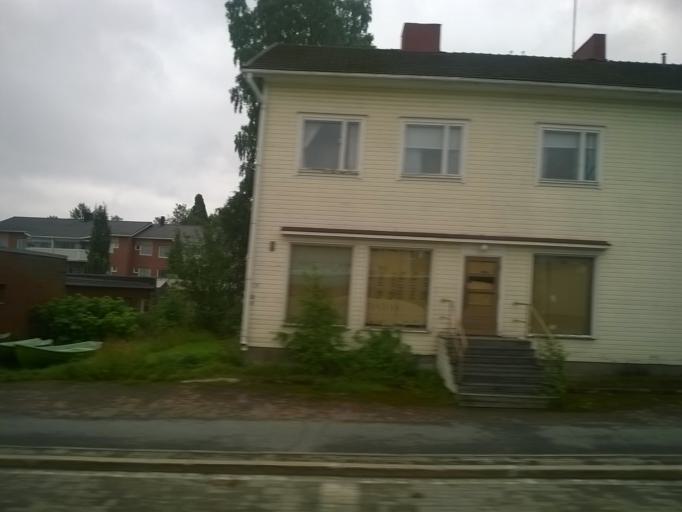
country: FI
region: Kainuu
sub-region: Kehys-Kainuu
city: Kuhmo
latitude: 64.1268
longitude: 29.5165
